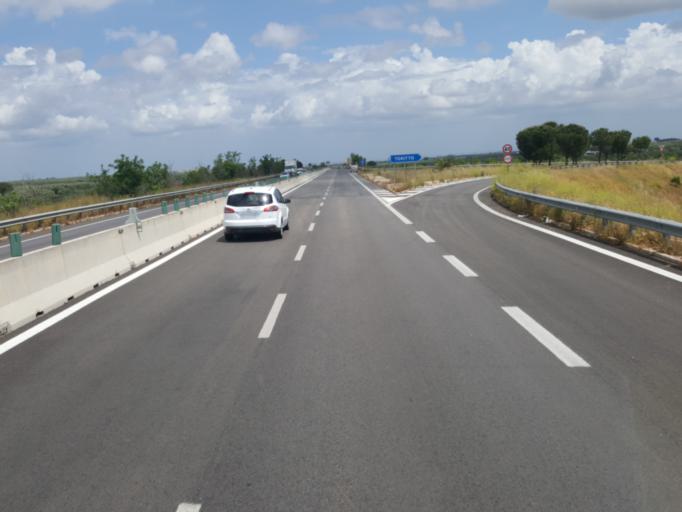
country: IT
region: Apulia
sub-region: Provincia di Bari
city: Toritto
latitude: 41.0063
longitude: 16.6727
